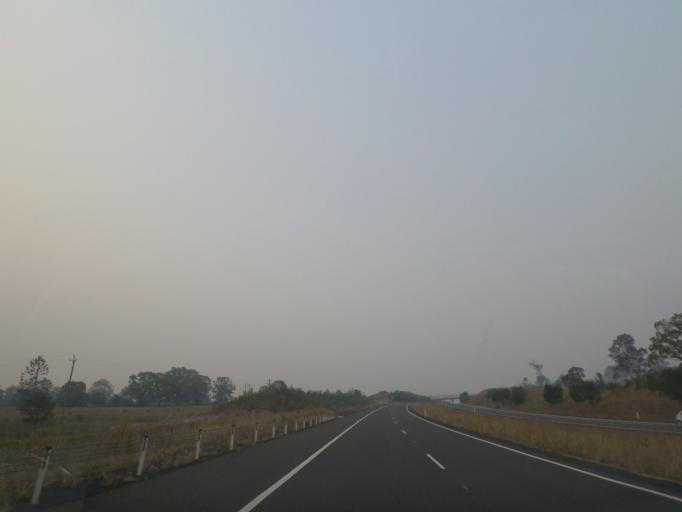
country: AU
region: New South Wales
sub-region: Nambucca Shire
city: Macksville
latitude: -30.7602
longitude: 152.9043
